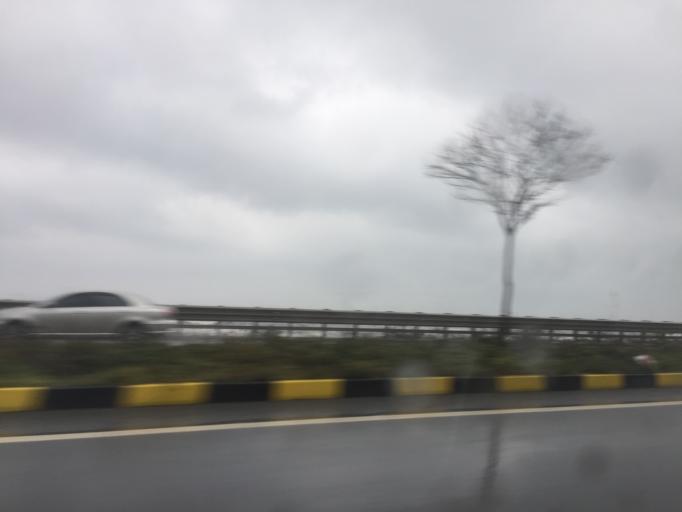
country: TR
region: Zonguldak
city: Alapli
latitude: 41.1150
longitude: 31.2922
